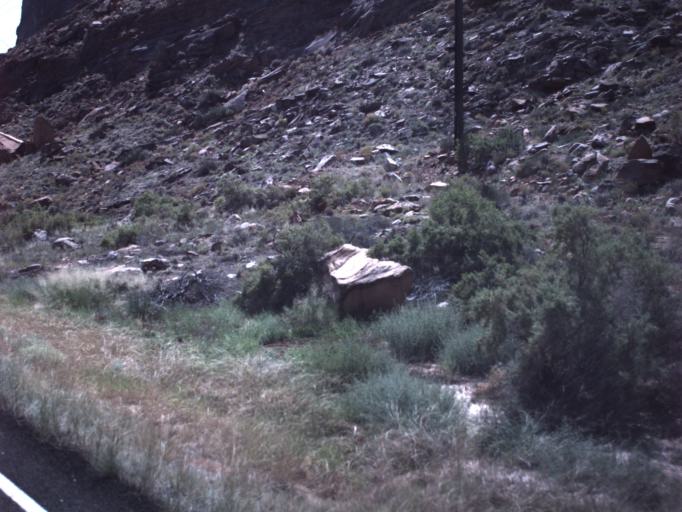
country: US
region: Utah
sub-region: Grand County
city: Moab
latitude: 38.5751
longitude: -109.5809
